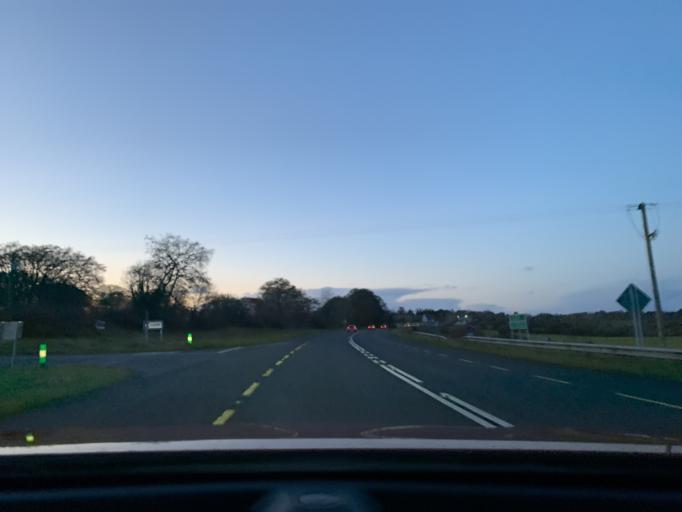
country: IE
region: Connaught
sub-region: County Leitrim
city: Carrick-on-Shannon
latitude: 53.9617
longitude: -8.1921
